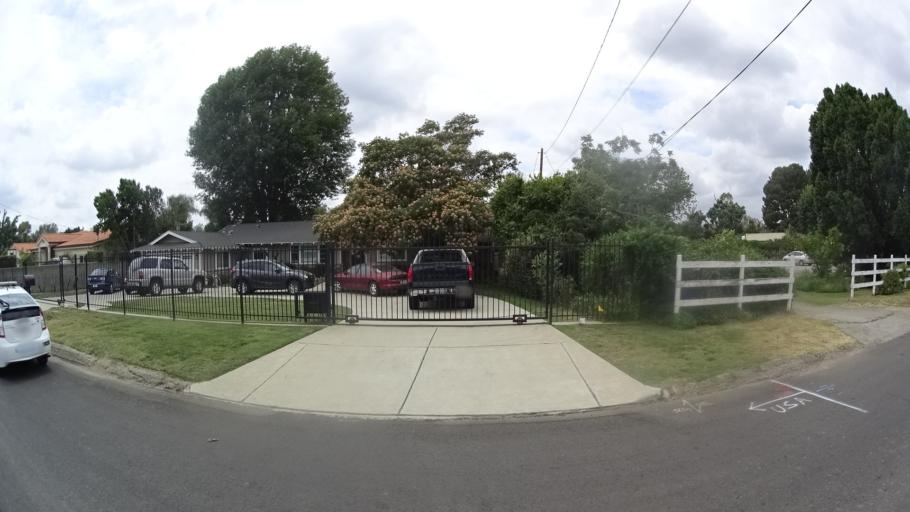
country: US
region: California
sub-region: Los Angeles County
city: San Fernando
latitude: 34.2460
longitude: -118.4631
